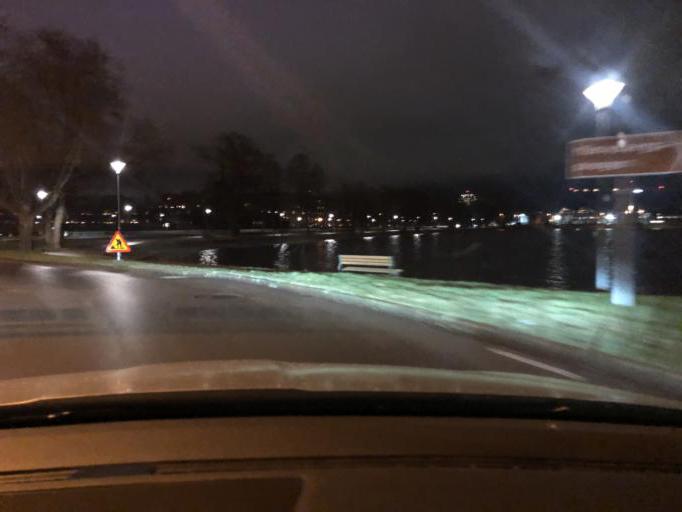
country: SE
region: Vaermland
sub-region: Karlstads Kommun
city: Karlstad
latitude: 59.3749
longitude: 13.4907
